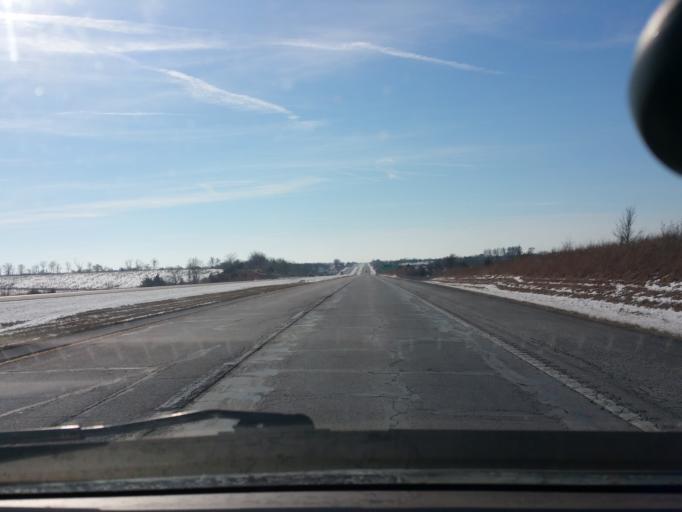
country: US
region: Iowa
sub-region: Decatur County
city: Lamoni
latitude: 40.4552
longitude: -93.9804
